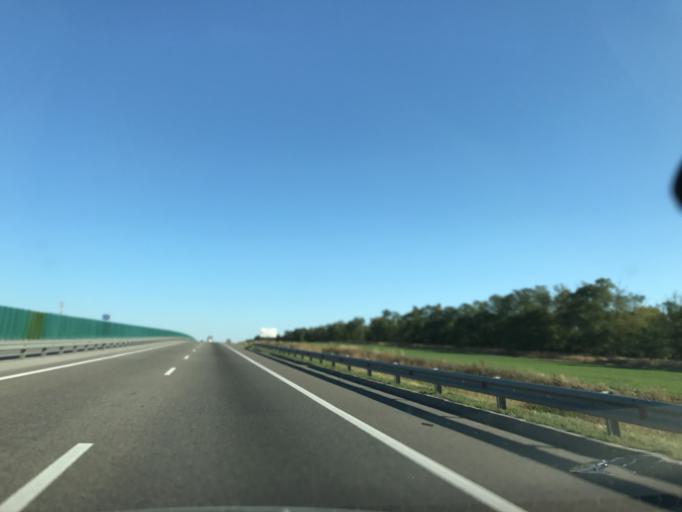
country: RU
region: Rostov
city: Glubokiy
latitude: 48.6196
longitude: 40.3555
